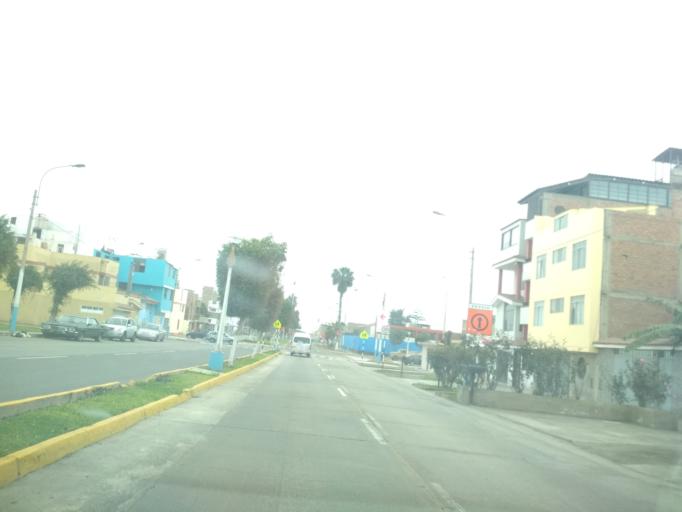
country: PE
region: Callao
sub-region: Callao
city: Callao
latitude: -12.0528
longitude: -77.1072
